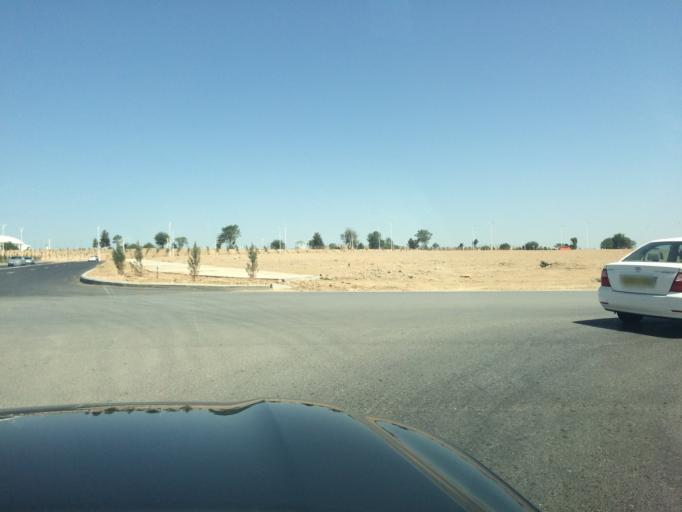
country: TM
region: Ahal
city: Ashgabat
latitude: 37.9224
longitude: 58.3585
